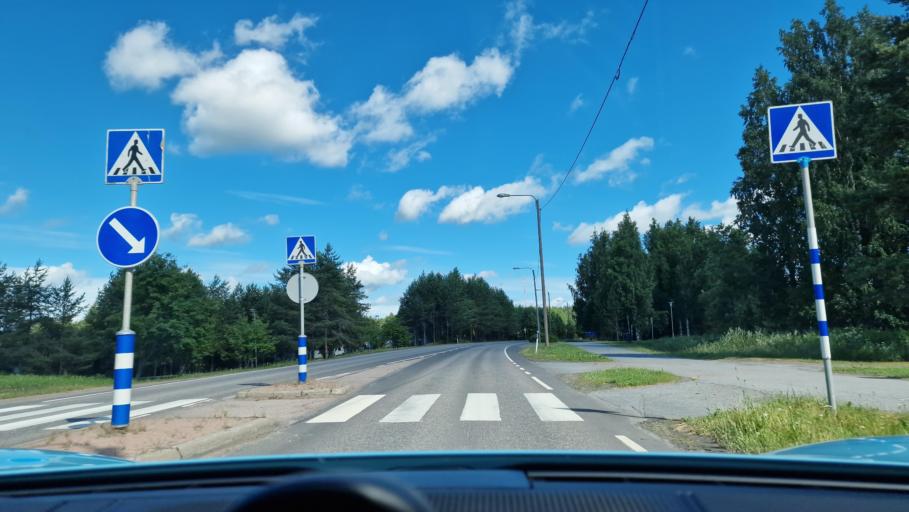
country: FI
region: Pirkanmaa
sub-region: Tampere
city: Orivesi
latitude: 61.6743
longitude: 24.3494
